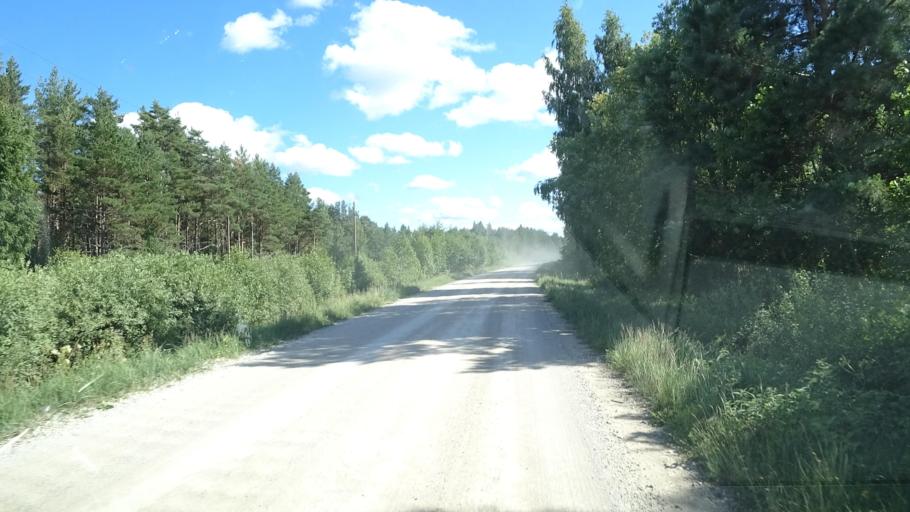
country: LV
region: Dundaga
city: Dundaga
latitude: 57.5953
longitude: 21.9824
